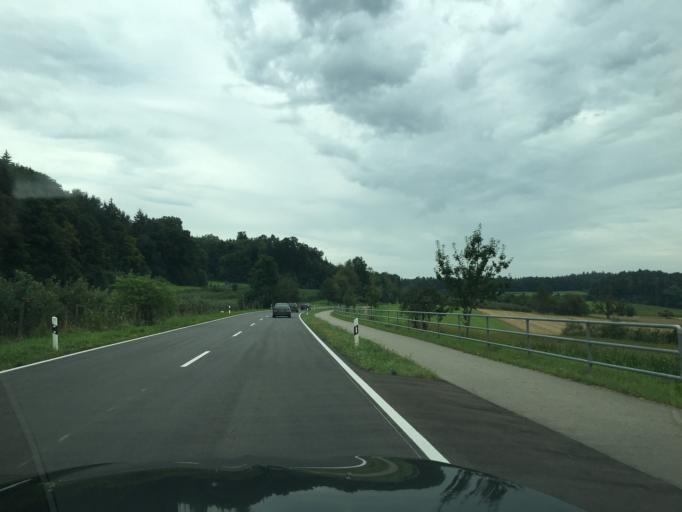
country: DE
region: Baden-Wuerttemberg
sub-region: Freiburg Region
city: Radolfzell am Bodensee
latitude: 47.7865
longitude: 8.9800
